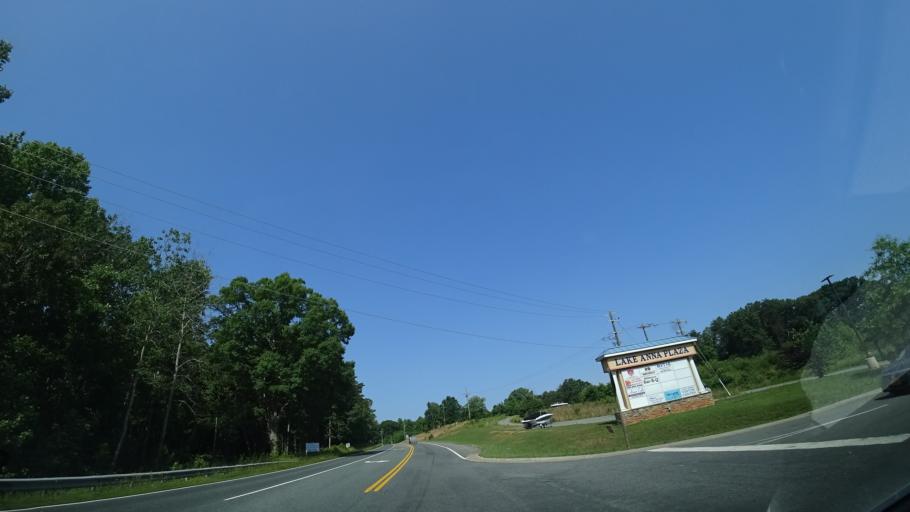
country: US
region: Virginia
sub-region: Louisa County
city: Louisa
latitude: 38.0848
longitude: -77.8237
